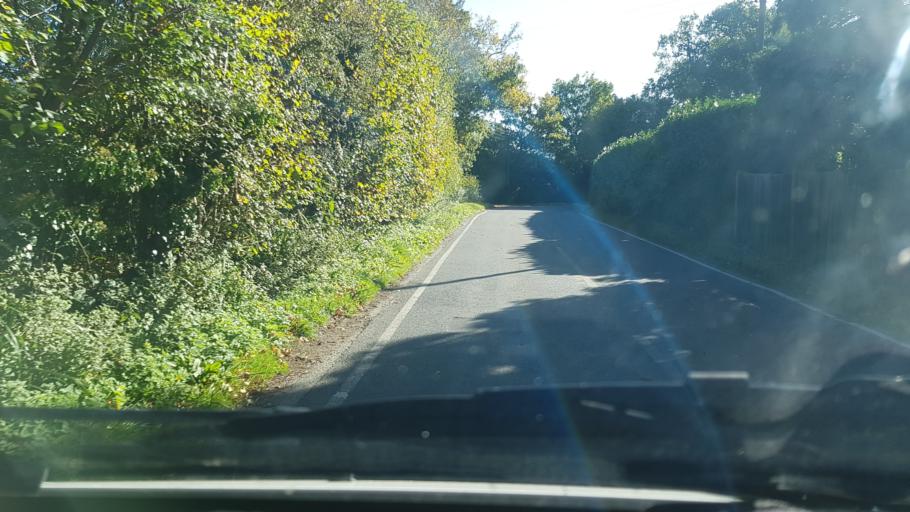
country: GB
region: England
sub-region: Surrey
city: Ockley
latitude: 51.1265
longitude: -0.3888
